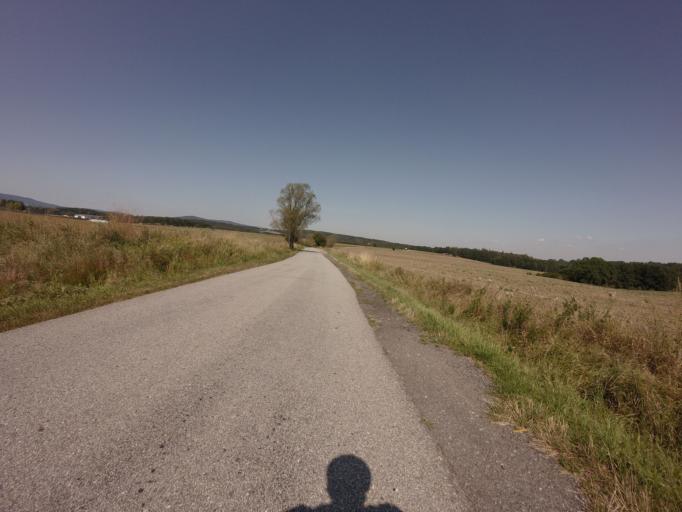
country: CZ
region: Jihocesky
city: Kamenny Ujezd
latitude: 48.9052
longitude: 14.4387
